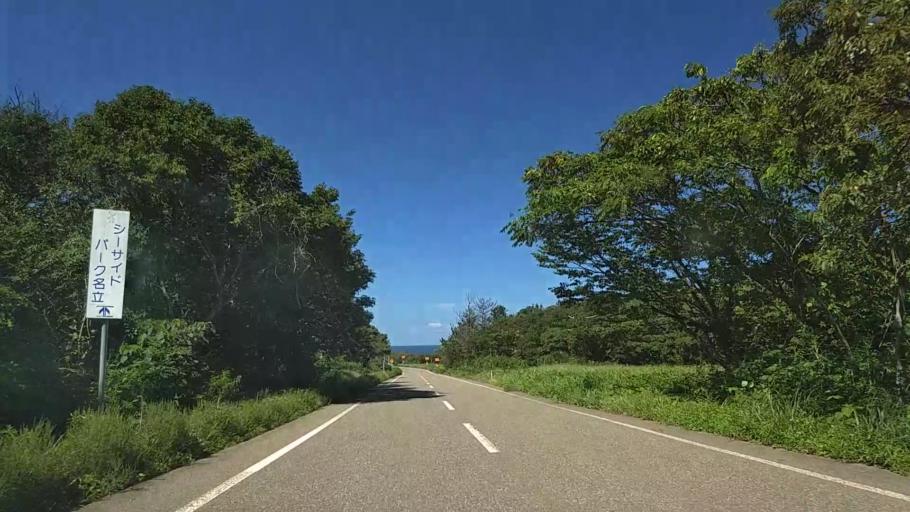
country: JP
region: Niigata
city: Joetsu
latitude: 37.1714
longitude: 138.1037
